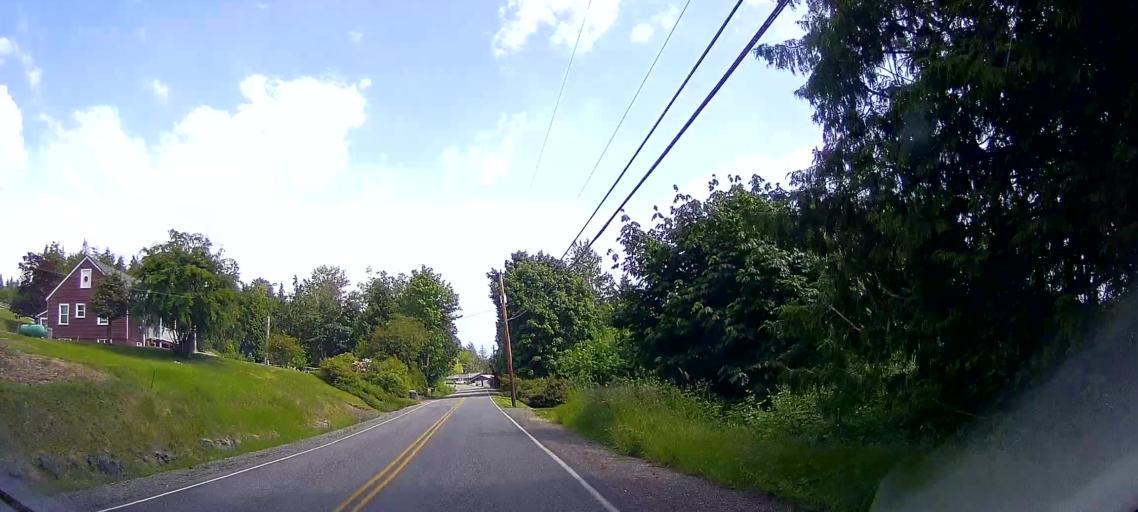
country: US
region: Washington
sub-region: Skagit County
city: Burlington
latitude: 48.5732
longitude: -122.3976
